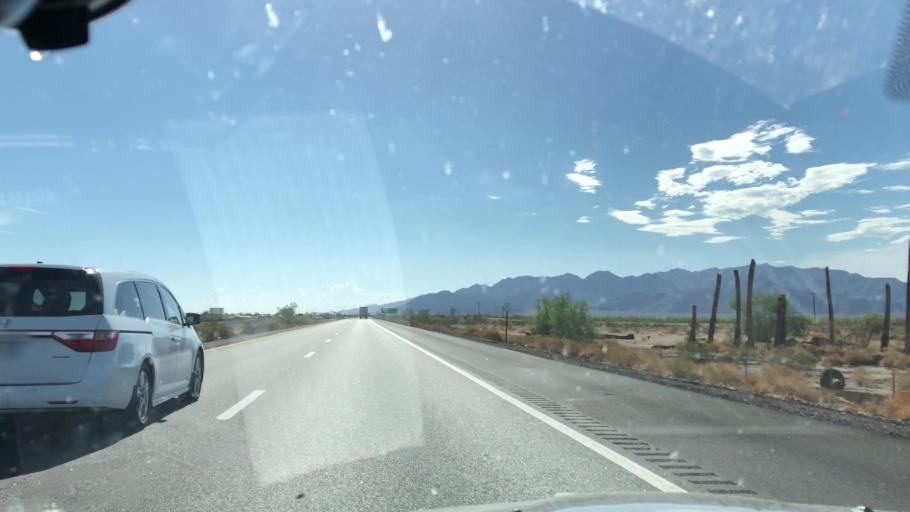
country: US
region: California
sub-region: Imperial County
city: Niland
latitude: 33.7106
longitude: -115.4081
